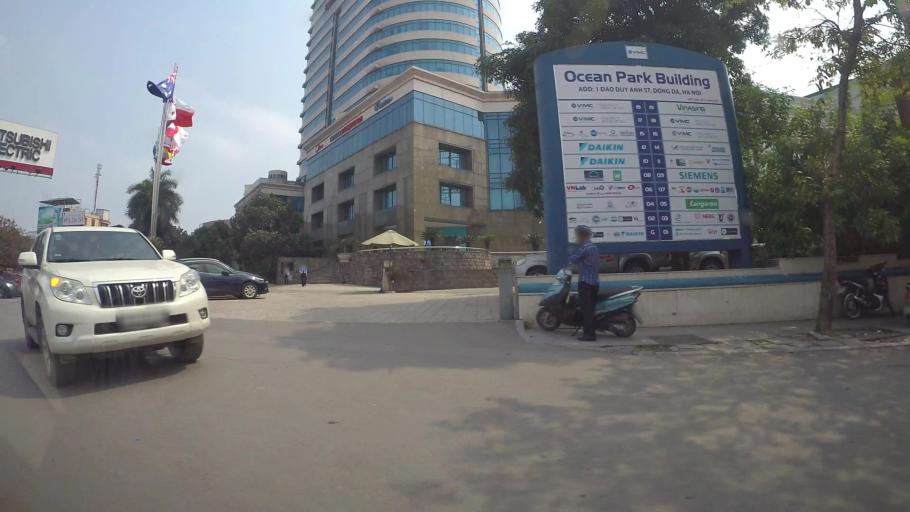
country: VN
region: Ha Noi
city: Hai BaTrung
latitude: 21.0078
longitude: 105.8402
